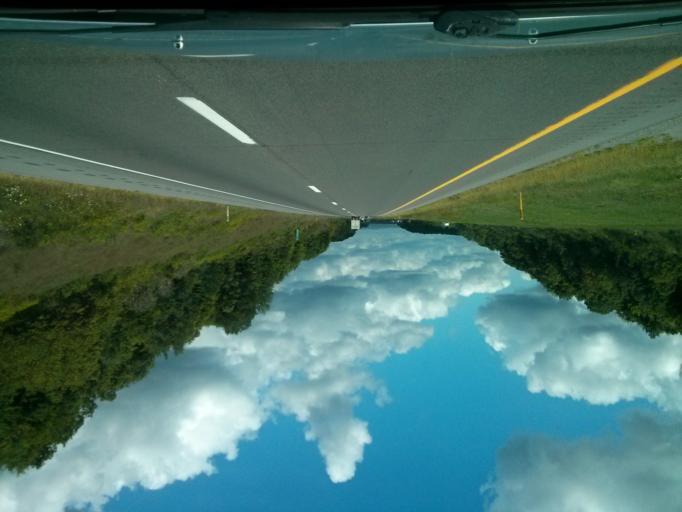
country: US
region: Pennsylvania
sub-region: Clearfield County
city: Treasure Lake
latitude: 41.1206
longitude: -78.6376
